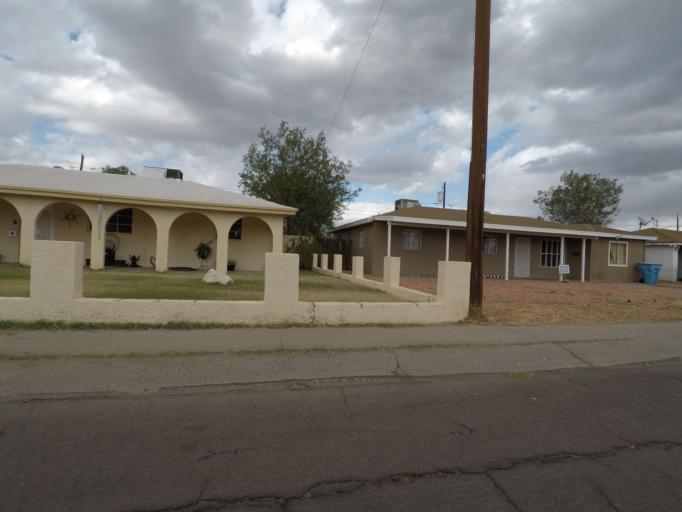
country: US
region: Arizona
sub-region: Maricopa County
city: Phoenix
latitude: 33.4971
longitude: -112.1223
